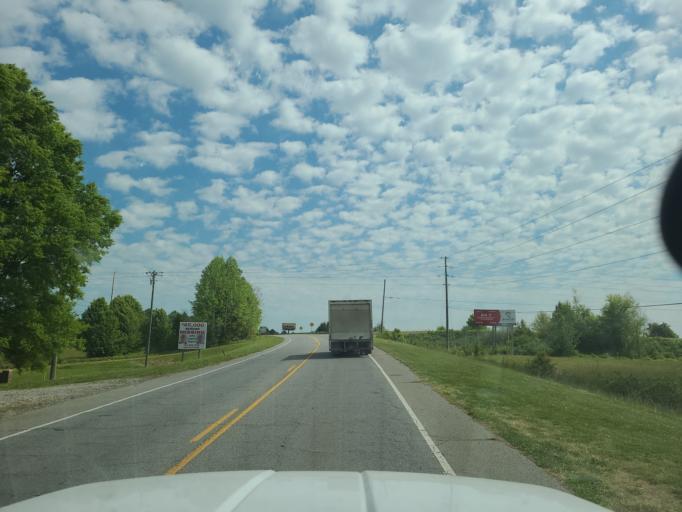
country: US
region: North Carolina
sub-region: Gaston County
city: Cherryville
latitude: 35.3548
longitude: -81.4395
